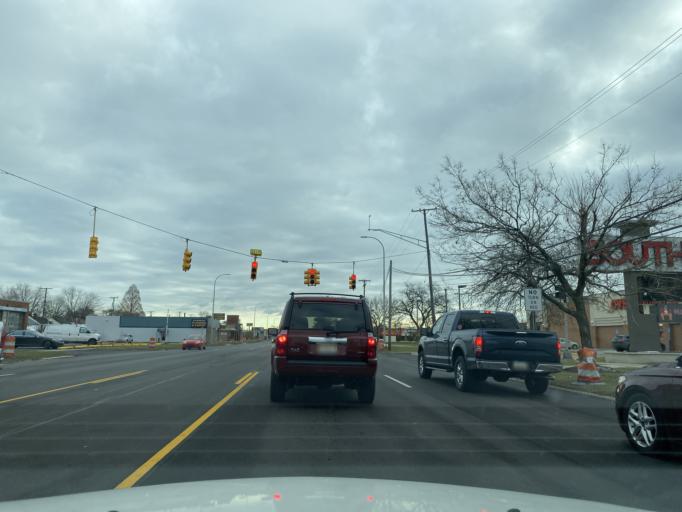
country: US
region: Michigan
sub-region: Wayne County
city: Southgate
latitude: 42.1993
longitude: -83.1898
